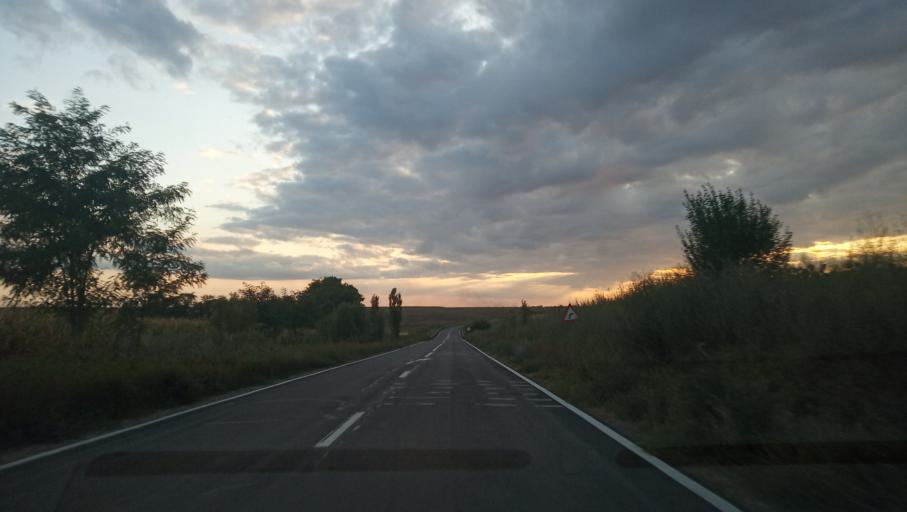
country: RO
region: Calarasi
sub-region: Comuna Vlad Tepes
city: Mihai Viteazu
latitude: 44.3607
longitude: 27.0224
